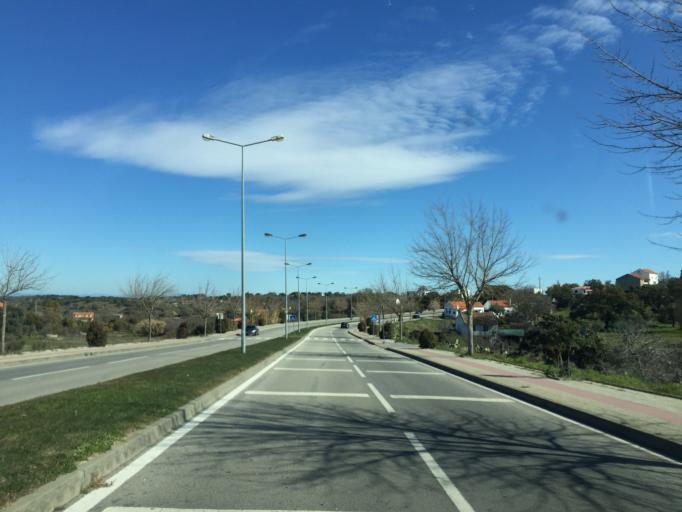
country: PT
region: Castelo Branco
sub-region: Castelo Branco
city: Castelo Branco
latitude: 39.8341
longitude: -7.4944
